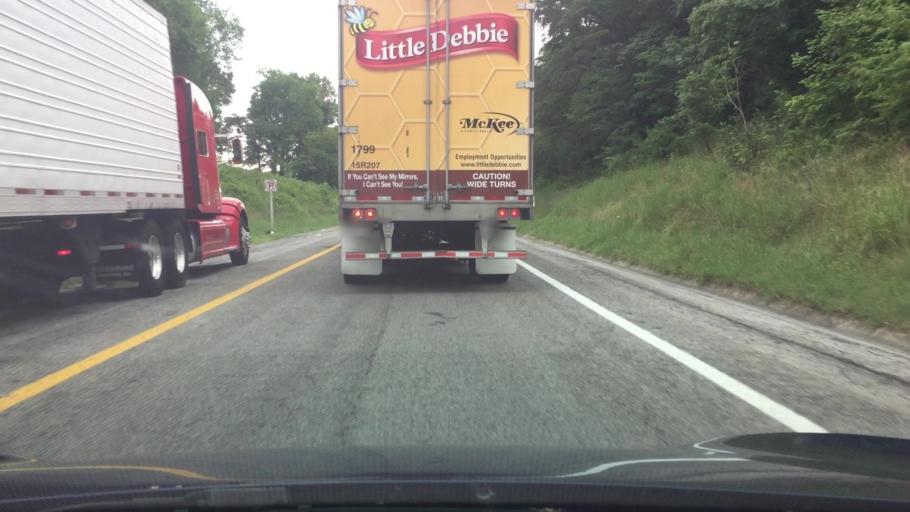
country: US
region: Virginia
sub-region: Montgomery County
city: Shawsville
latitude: 37.2562
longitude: -80.1746
